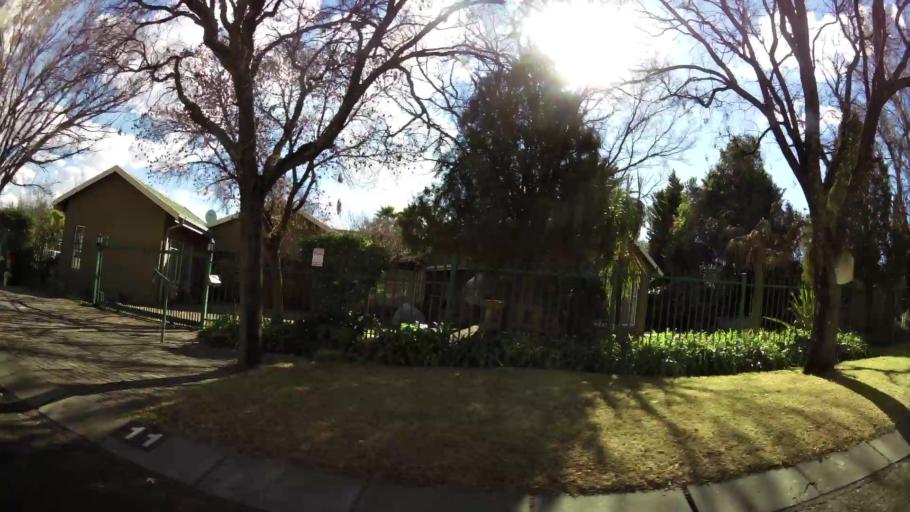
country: ZA
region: North-West
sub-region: Dr Kenneth Kaunda District Municipality
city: Klerksdorp
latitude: -26.8437
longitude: 26.6457
